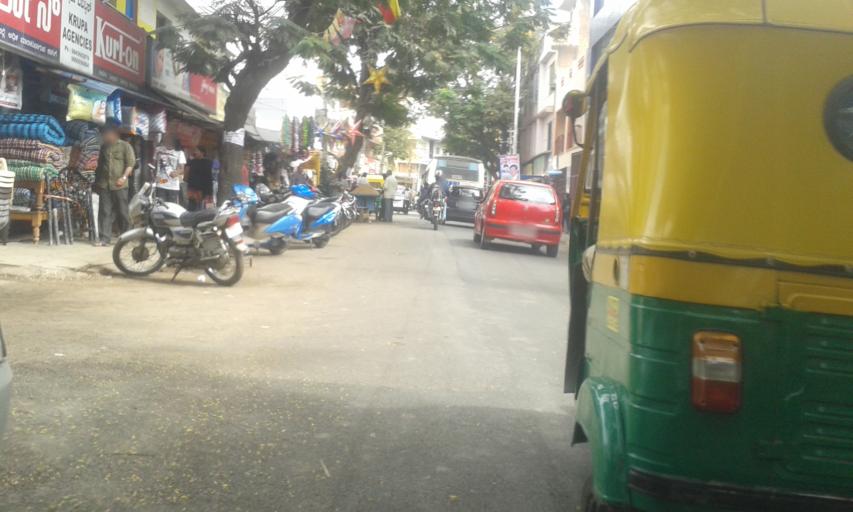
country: IN
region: Karnataka
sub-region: Bangalore Urban
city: Bangalore
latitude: 12.9723
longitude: 77.6501
